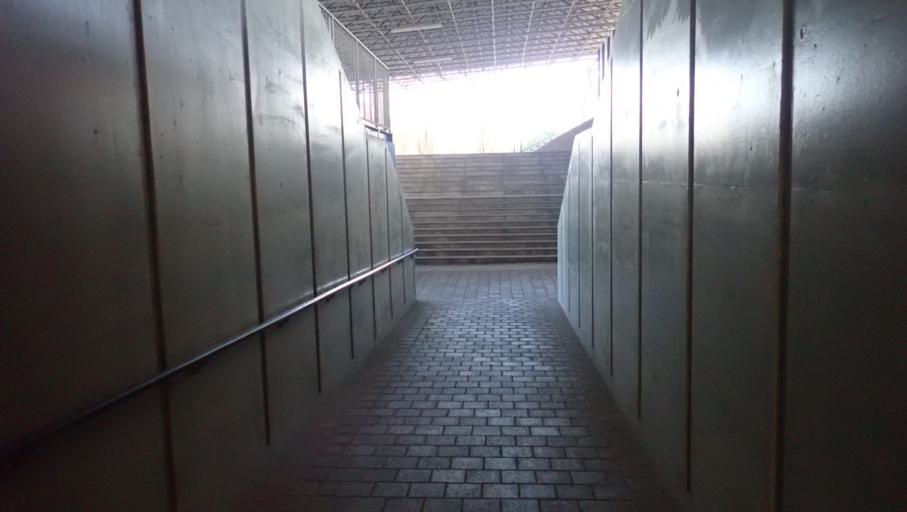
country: BE
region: Flanders
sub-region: Provincie Antwerpen
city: Brecht
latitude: 51.3572
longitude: 4.6327
